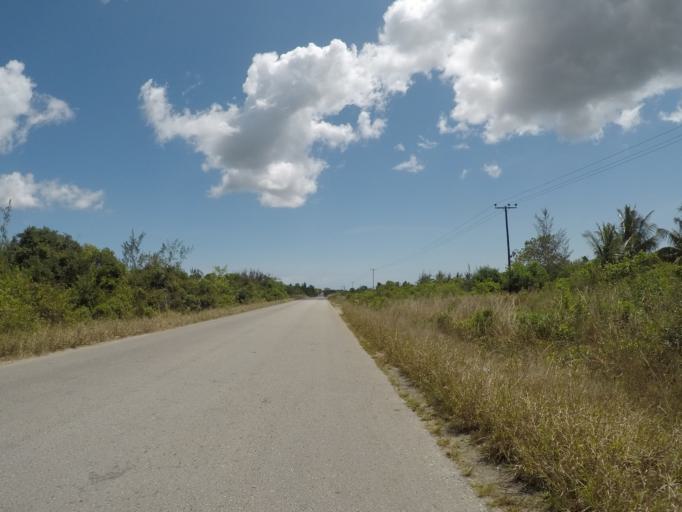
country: TZ
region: Zanzibar Central/South
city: Nganane
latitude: -6.2767
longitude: 39.4842
